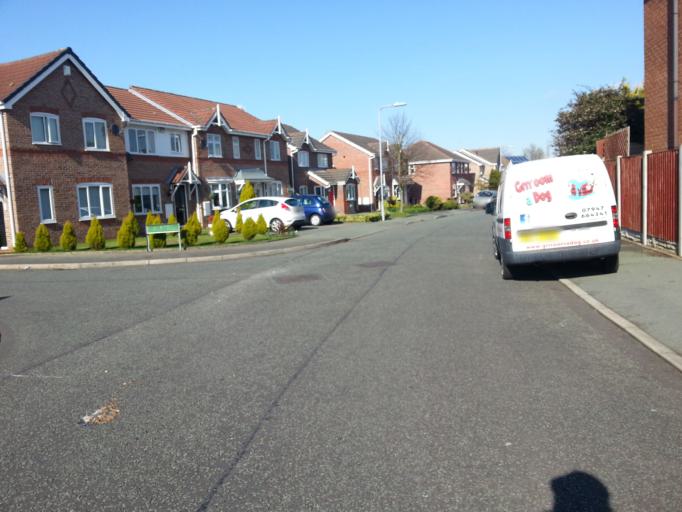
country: GB
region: England
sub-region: Knowsley
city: Huyton
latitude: 53.3694
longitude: -2.8389
